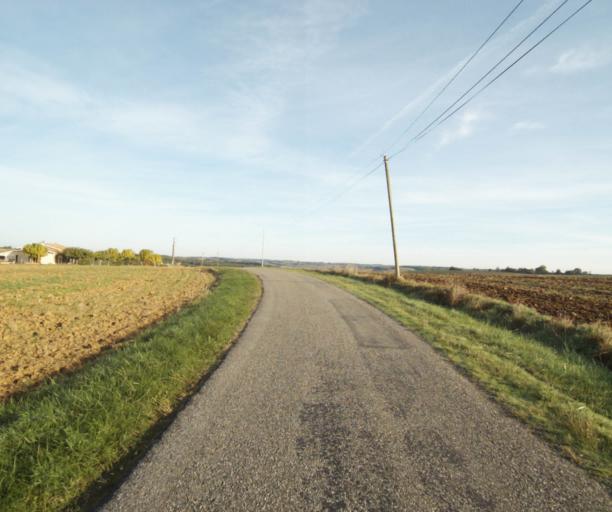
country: FR
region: Midi-Pyrenees
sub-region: Departement du Tarn-et-Garonne
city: Nohic
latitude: 43.9181
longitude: 1.4813
